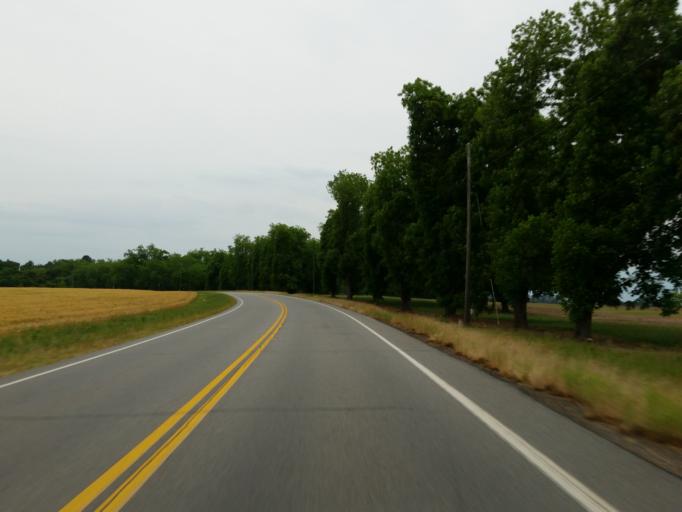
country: US
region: Georgia
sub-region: Dooly County
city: Unadilla
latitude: 32.2305
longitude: -83.7565
